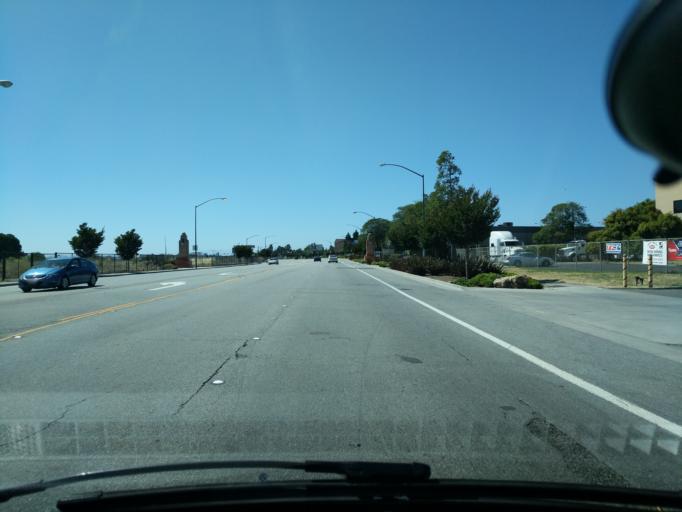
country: US
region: California
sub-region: Alameda County
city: San Leandro
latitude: 37.7233
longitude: -122.1956
